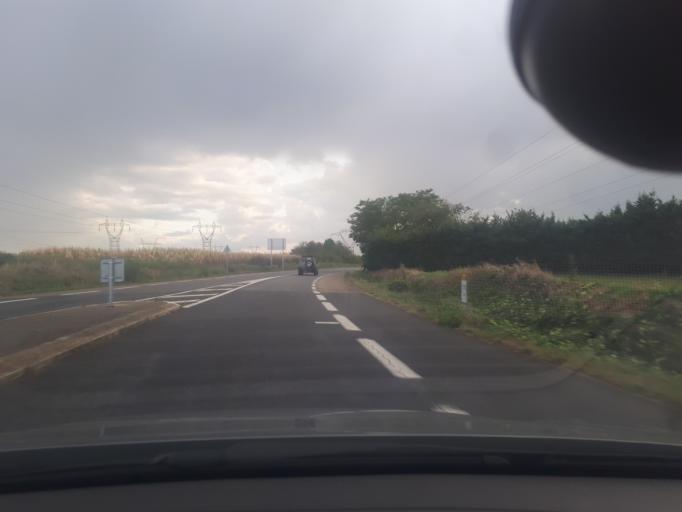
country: FR
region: Rhone-Alpes
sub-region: Departement du Rhone
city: Saint-Bonnet-de-Mure
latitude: 45.7262
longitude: 5.0288
